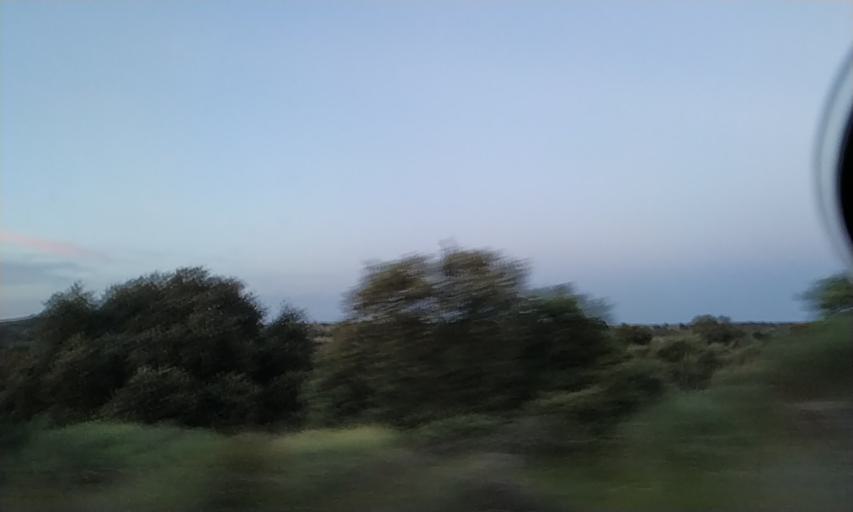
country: ES
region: Extremadura
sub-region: Provincia de Caceres
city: Piedras Albas
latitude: 39.7647
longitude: -6.9097
